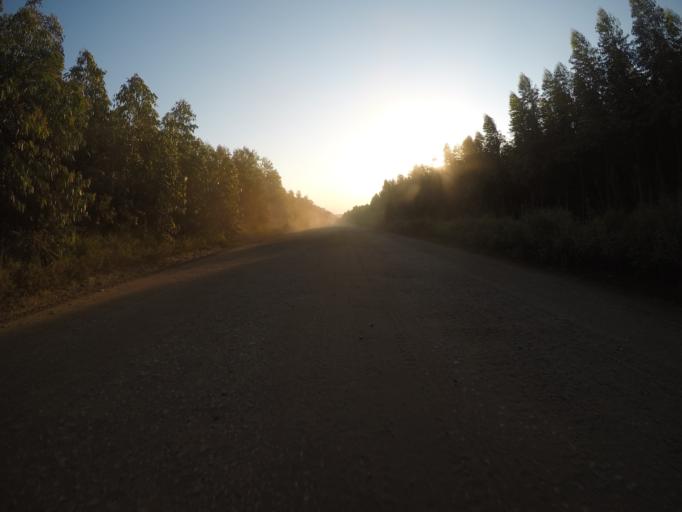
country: ZA
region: KwaZulu-Natal
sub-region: uThungulu District Municipality
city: KwaMbonambi
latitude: -28.6676
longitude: 32.0715
